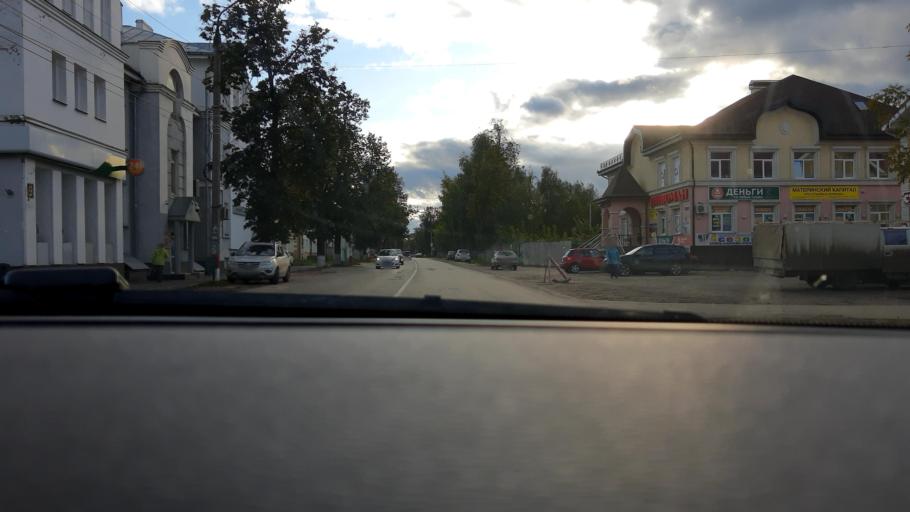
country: RU
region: Nizjnij Novgorod
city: Novaya Balakhna
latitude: 56.4912
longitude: 43.6086
